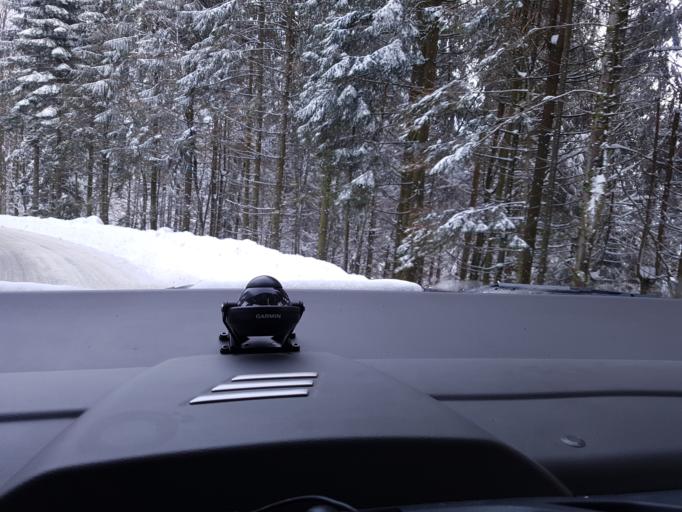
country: FR
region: Alsace
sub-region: Departement du Bas-Rhin
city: Ville
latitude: 48.3830
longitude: 7.2591
